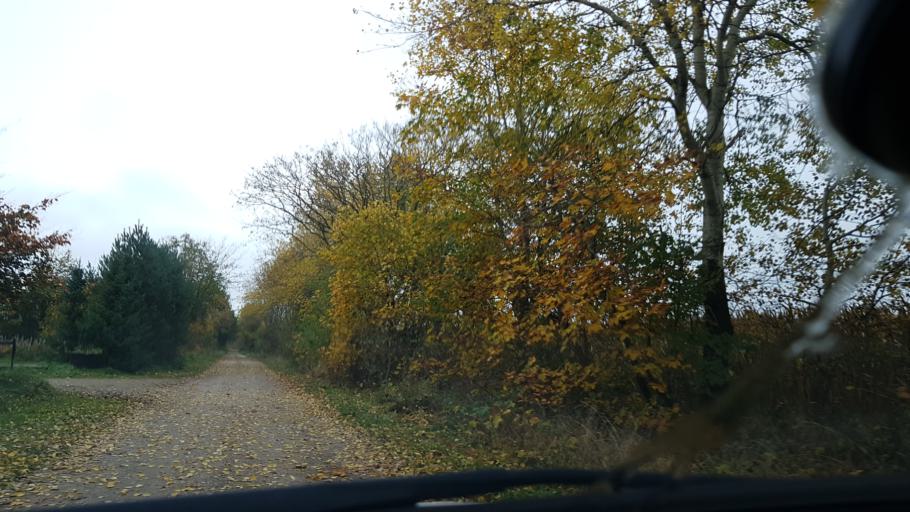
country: DK
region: South Denmark
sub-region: Esbjerg Kommune
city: Ribe
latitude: 55.2997
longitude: 8.8126
